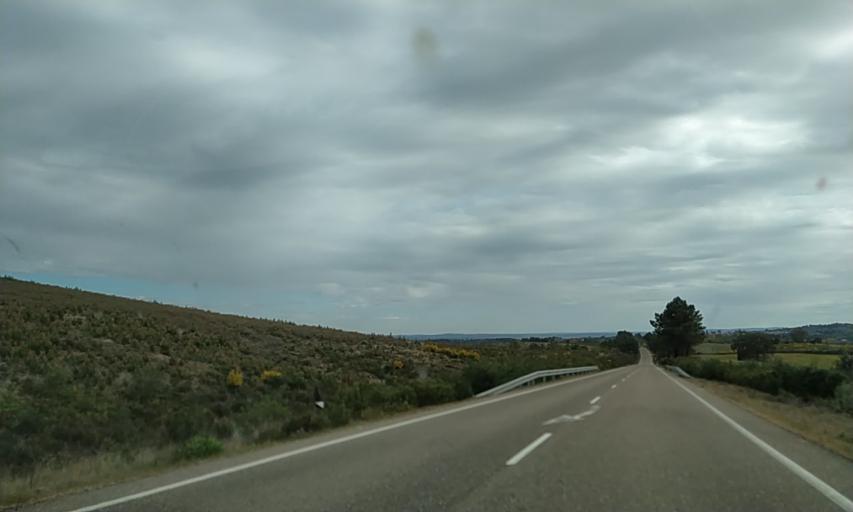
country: ES
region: Extremadura
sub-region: Provincia de Caceres
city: Perales del Puerto
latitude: 40.1948
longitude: -6.6761
